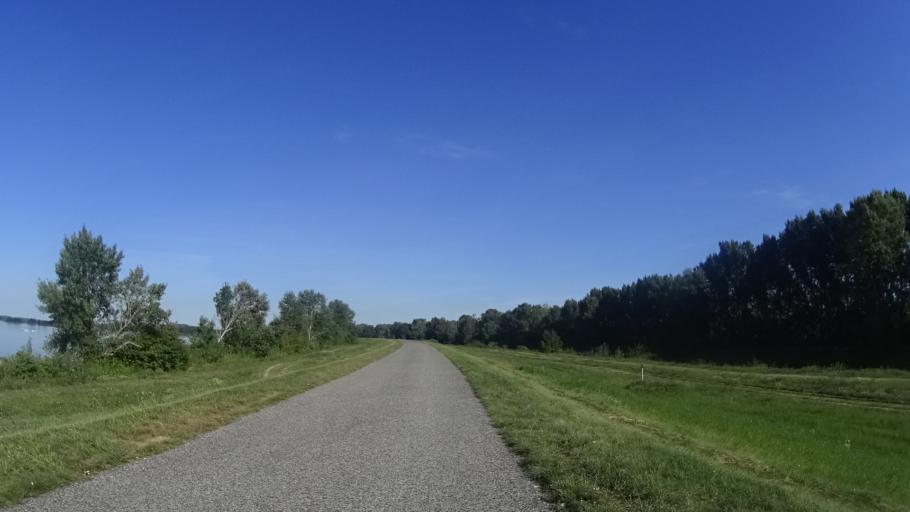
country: SK
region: Bratislavsky
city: Dunajska Luzna
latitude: 48.0519
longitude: 17.2355
